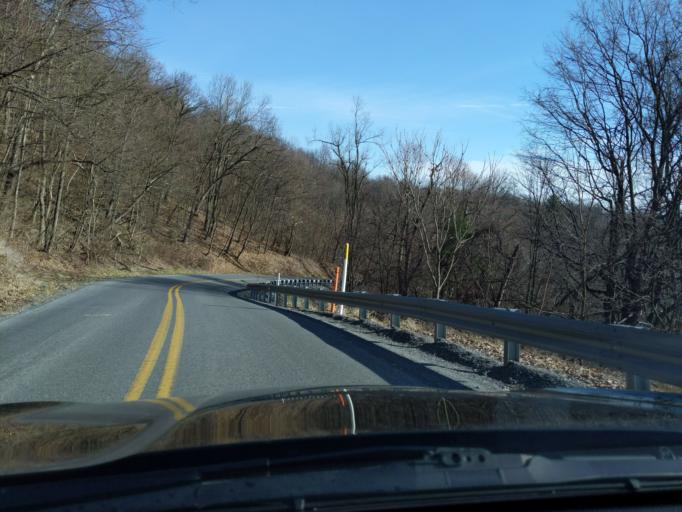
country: US
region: Pennsylvania
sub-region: Blair County
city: Williamsburg
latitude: 40.4200
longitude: -78.2885
